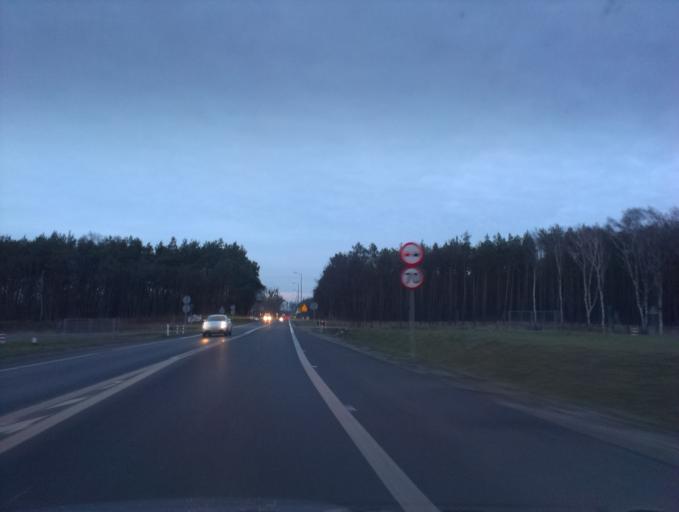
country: PL
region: Greater Poland Voivodeship
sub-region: Powiat poznanski
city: Zlotniki
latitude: 52.5278
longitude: 16.8335
